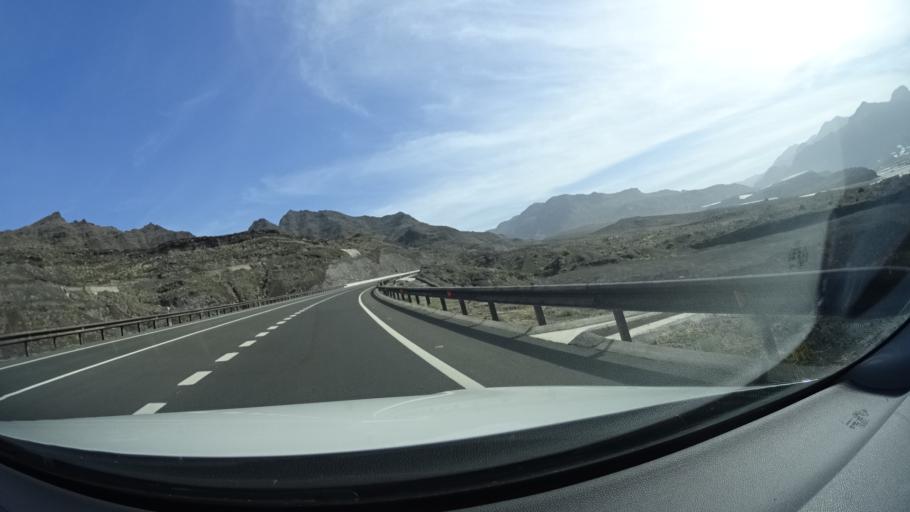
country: ES
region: Canary Islands
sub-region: Provincia de Las Palmas
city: San Nicolas
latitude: 28.0056
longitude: -15.8064
